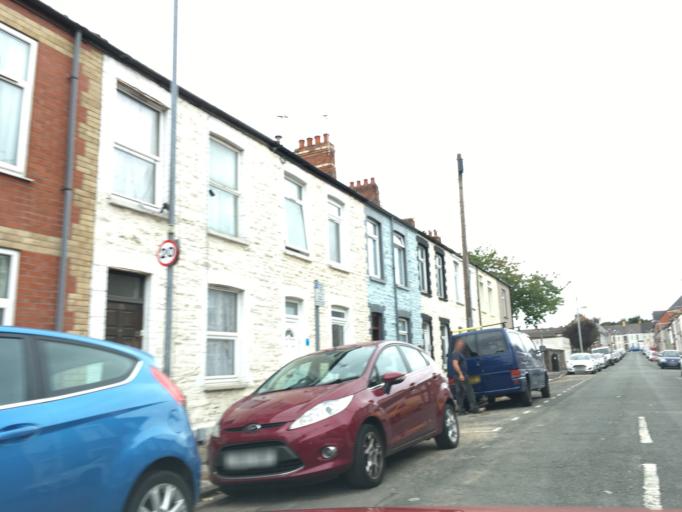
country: GB
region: Wales
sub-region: Cardiff
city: Cardiff
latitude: 51.4955
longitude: -3.1765
